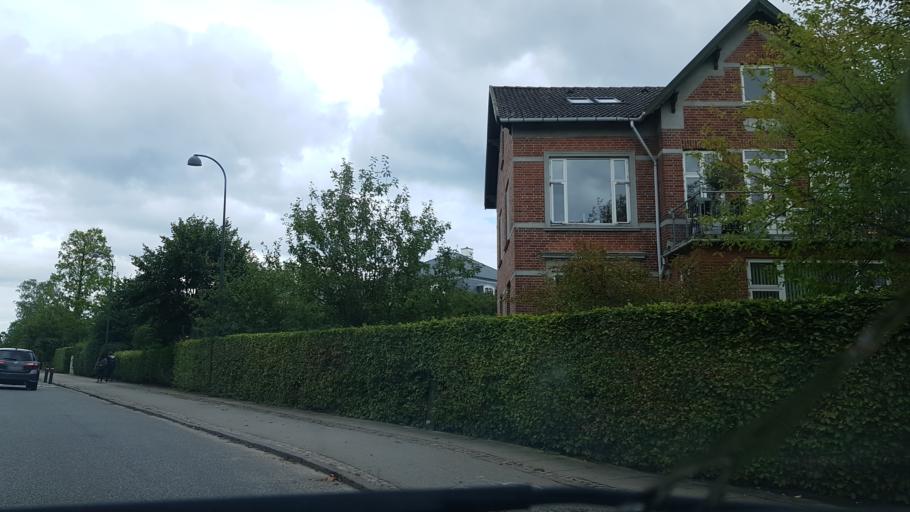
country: DK
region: Capital Region
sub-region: Gentofte Kommune
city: Charlottenlund
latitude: 55.7563
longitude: 12.5786
